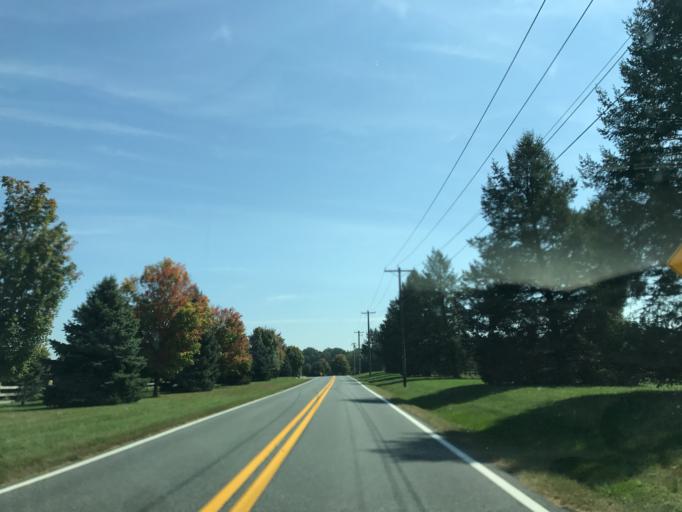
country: US
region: Delaware
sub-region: New Castle County
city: Middletown
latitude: 39.5081
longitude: -75.8013
